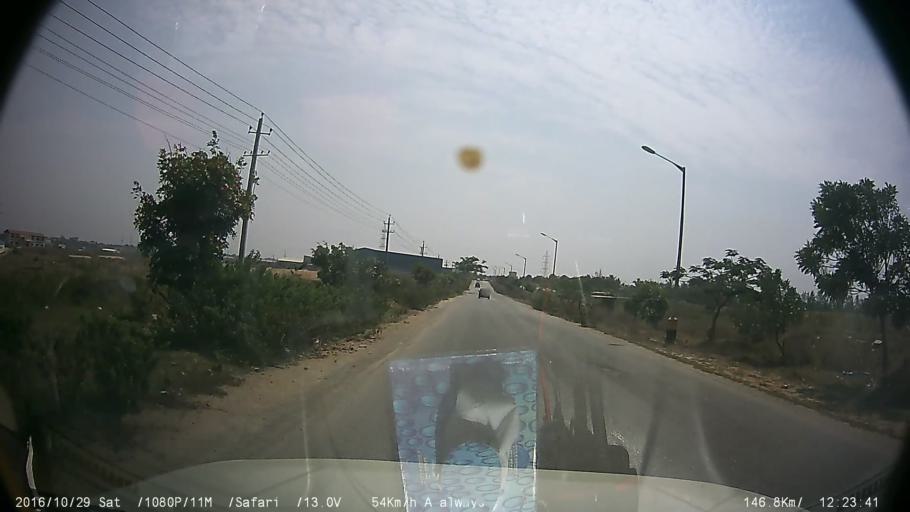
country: IN
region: Karnataka
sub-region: Mysore
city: Mysore
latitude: 12.3588
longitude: 76.5628
